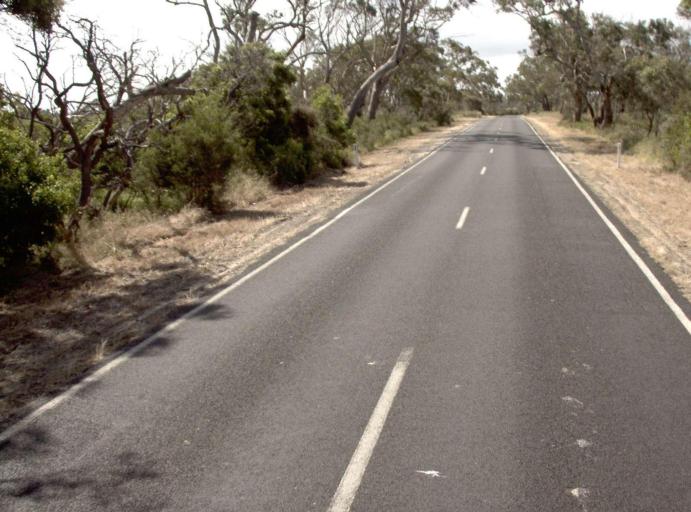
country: AU
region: Victoria
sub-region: Wellington
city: Sale
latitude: -38.3218
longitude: 147.1585
